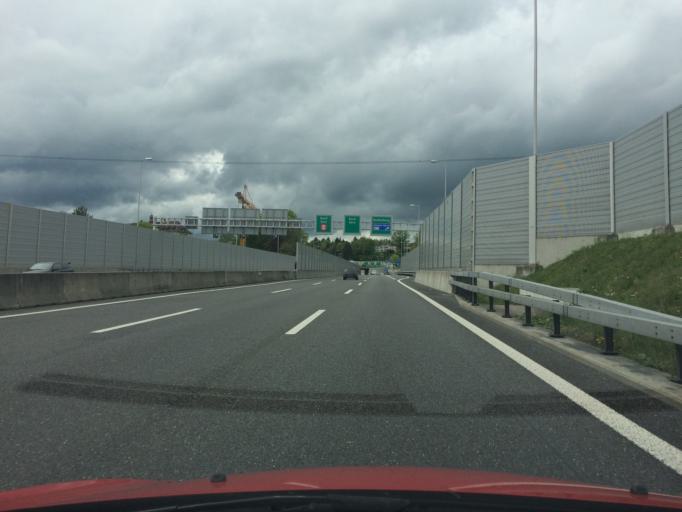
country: CH
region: Lucerne
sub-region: Hochdorf District
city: Emmen
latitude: 47.0830
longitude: 8.2788
